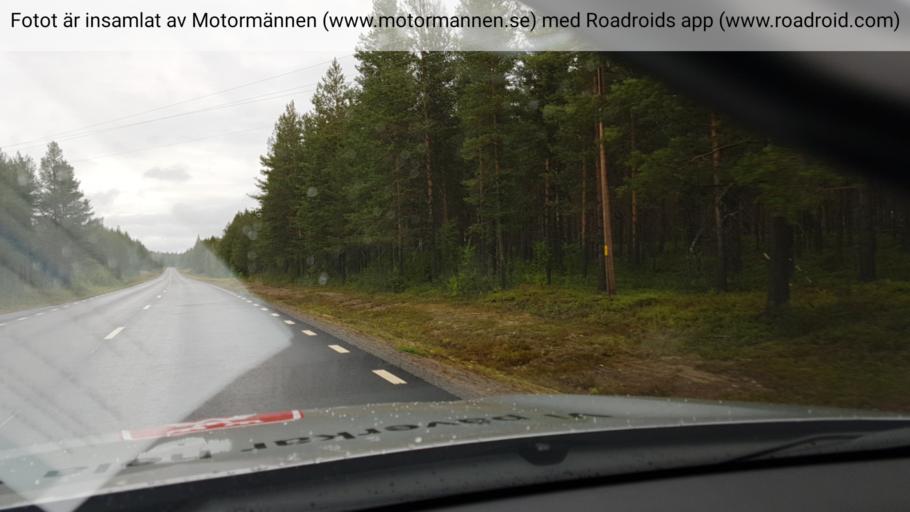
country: SE
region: Norrbotten
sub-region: Alvsbyns Kommun
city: AElvsbyn
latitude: 66.2526
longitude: 20.8506
